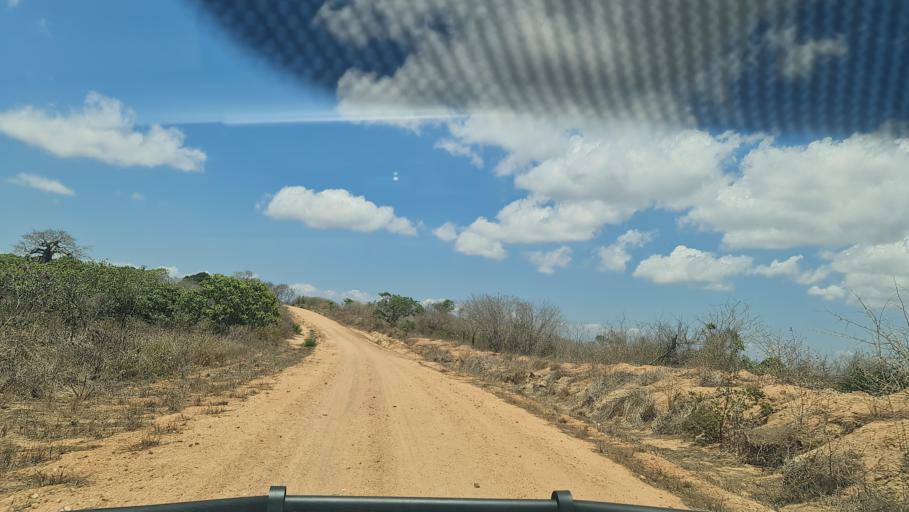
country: MZ
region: Nampula
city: Nacala
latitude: -14.3238
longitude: 40.5874
